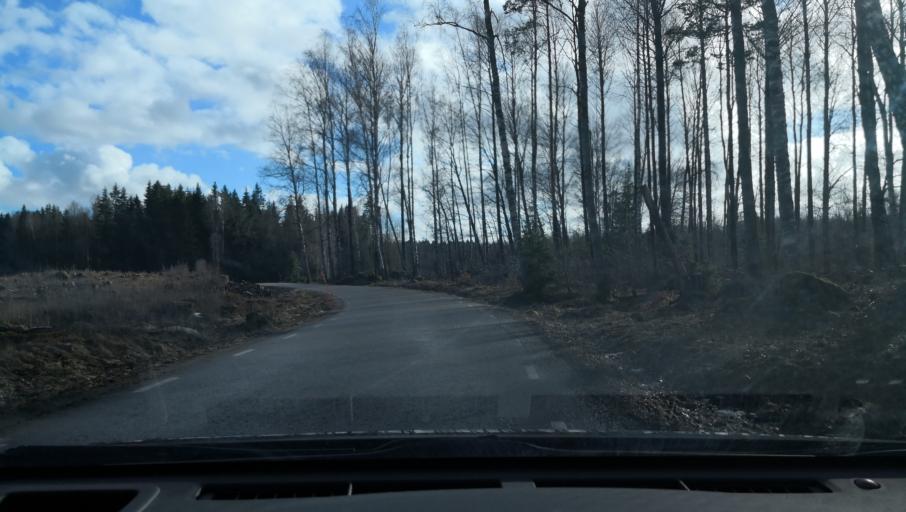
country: SE
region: Vaestmanland
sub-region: Arboga Kommun
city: Arboga
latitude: 59.3213
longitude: 15.7585
